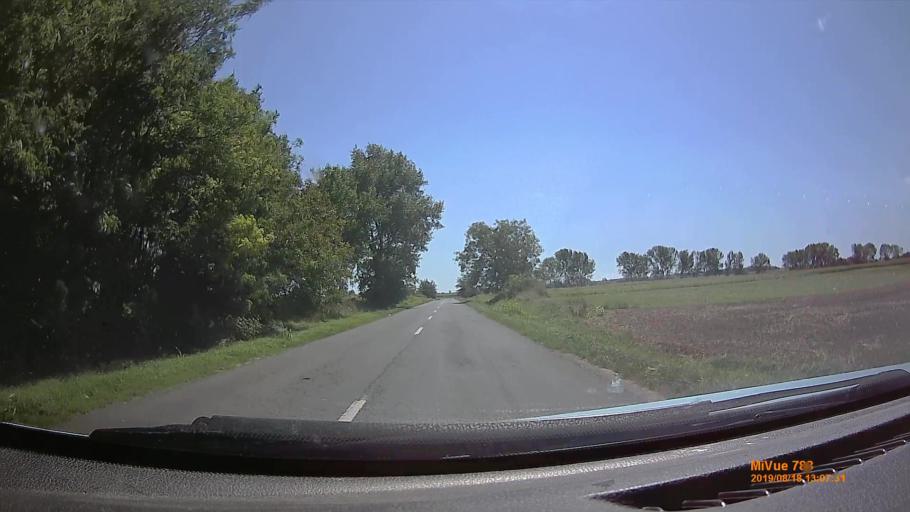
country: HU
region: Fejer
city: Kaloz
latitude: 46.9491
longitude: 18.4954
